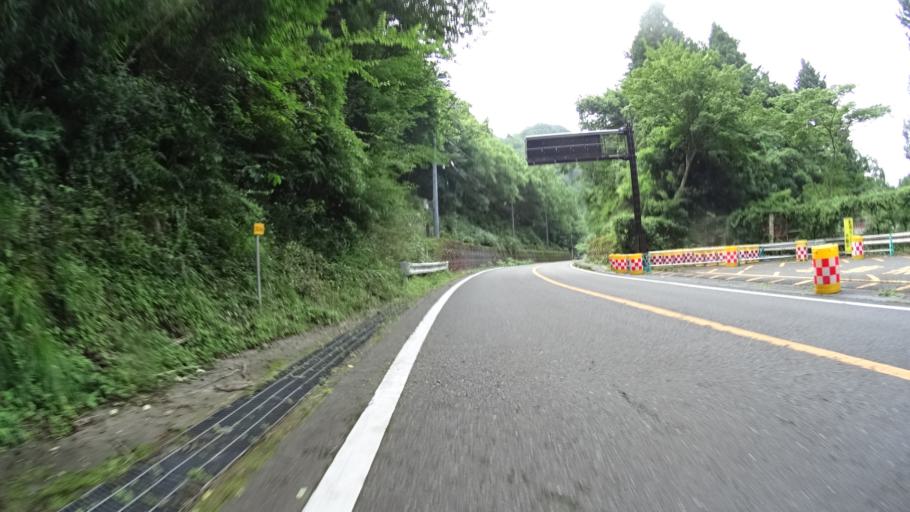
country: JP
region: Kanagawa
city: Hadano
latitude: 35.5024
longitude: 139.2302
